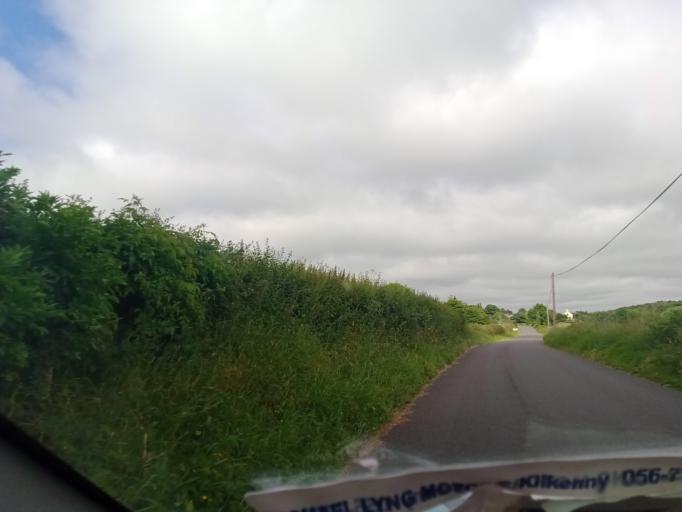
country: IE
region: Leinster
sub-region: Kilkenny
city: Ballyragget
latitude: 52.7649
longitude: -7.4652
